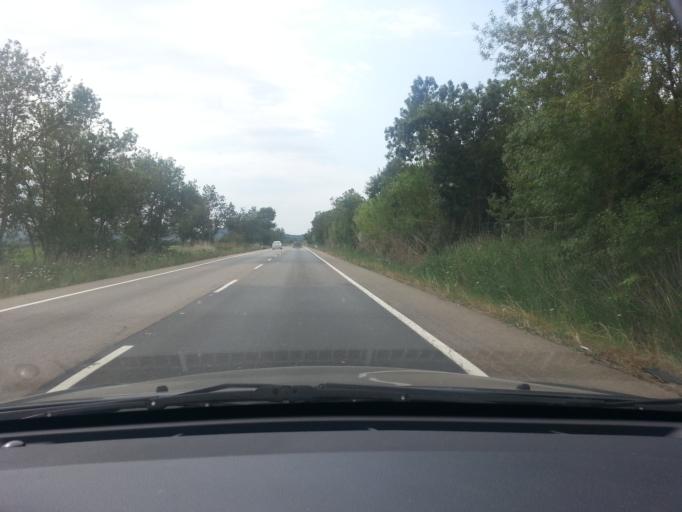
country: ES
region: Catalonia
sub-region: Provincia de Girona
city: Torroella de Montgri
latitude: 42.0120
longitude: 3.1438
